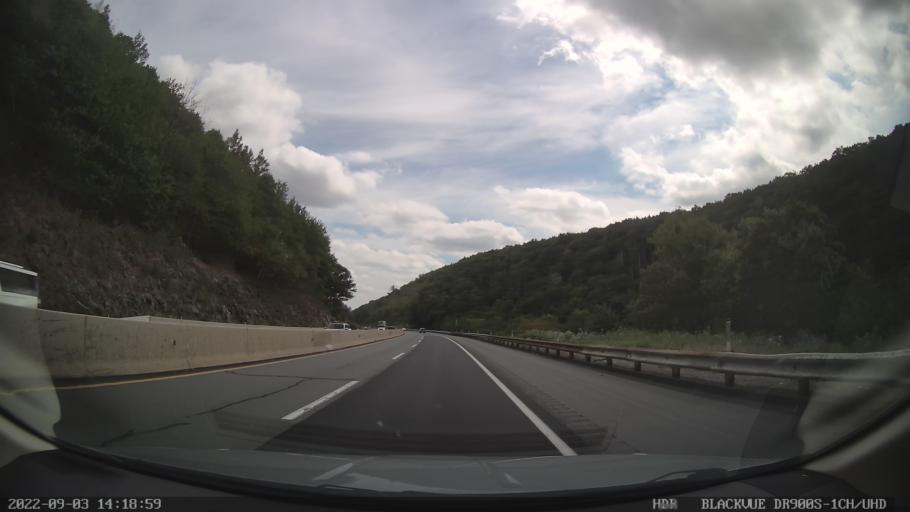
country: US
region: Pennsylvania
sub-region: Carbon County
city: Weissport East
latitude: 40.9093
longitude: -75.6452
